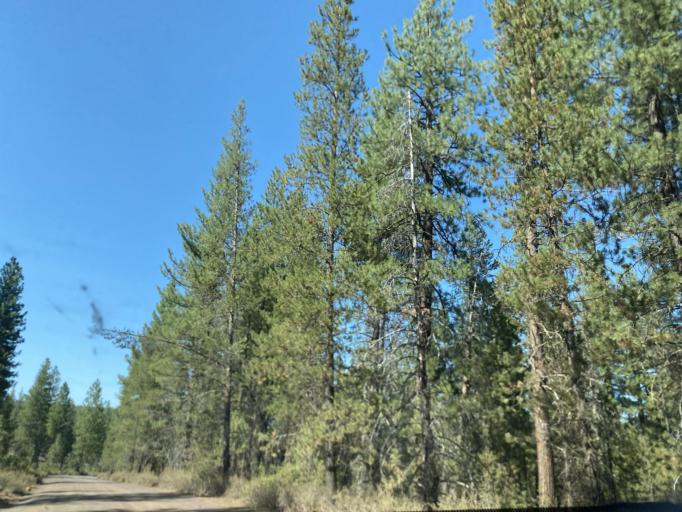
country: US
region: Oregon
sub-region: Deschutes County
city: Sunriver
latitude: 43.8769
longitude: -121.4665
